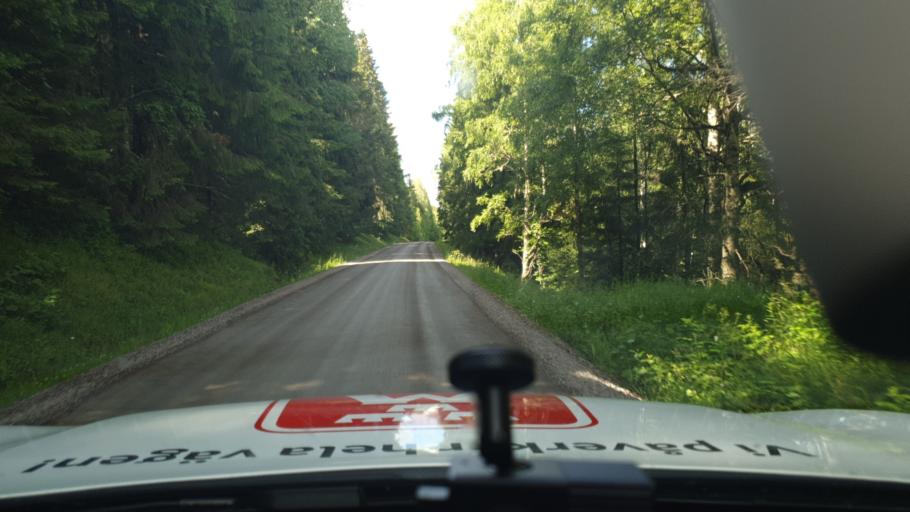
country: SE
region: Vaermland
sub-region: Hagfors Kommun
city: Ekshaerad
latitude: 60.4196
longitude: 13.2501
